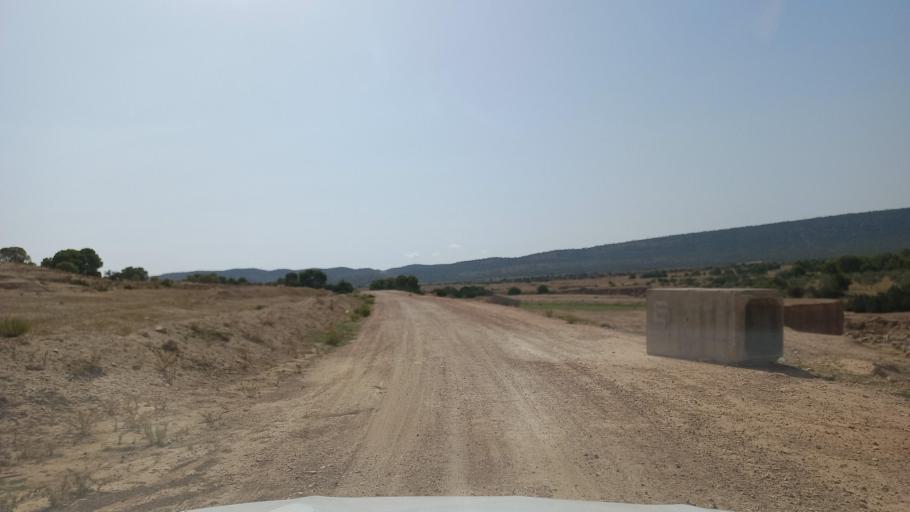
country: TN
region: Al Qasrayn
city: Sbiba
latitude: 35.3971
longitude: 8.9492
